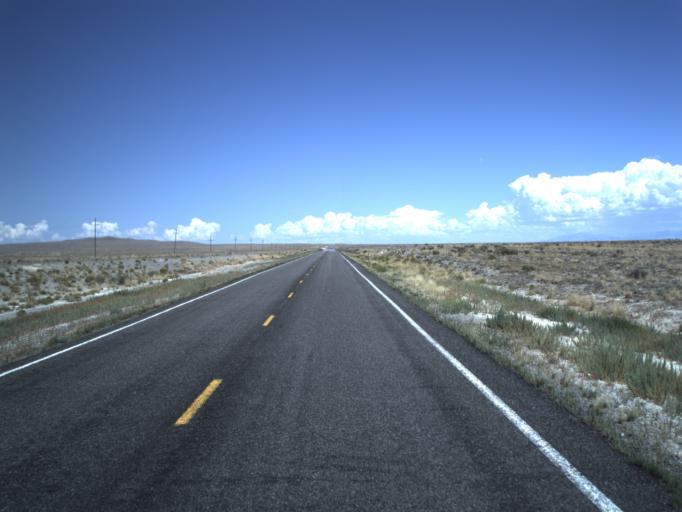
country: US
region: Utah
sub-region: Millard County
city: Delta
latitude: 39.1113
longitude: -113.1358
